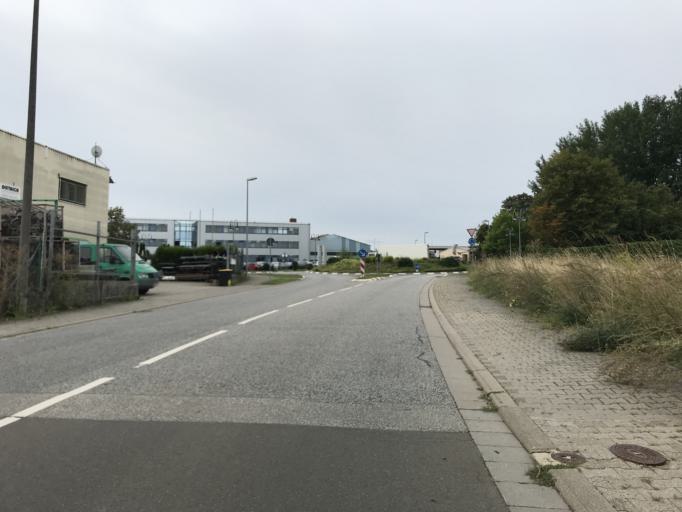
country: DE
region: Rheinland-Pfalz
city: Zotzenheim
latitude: 49.8624
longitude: 7.9737
